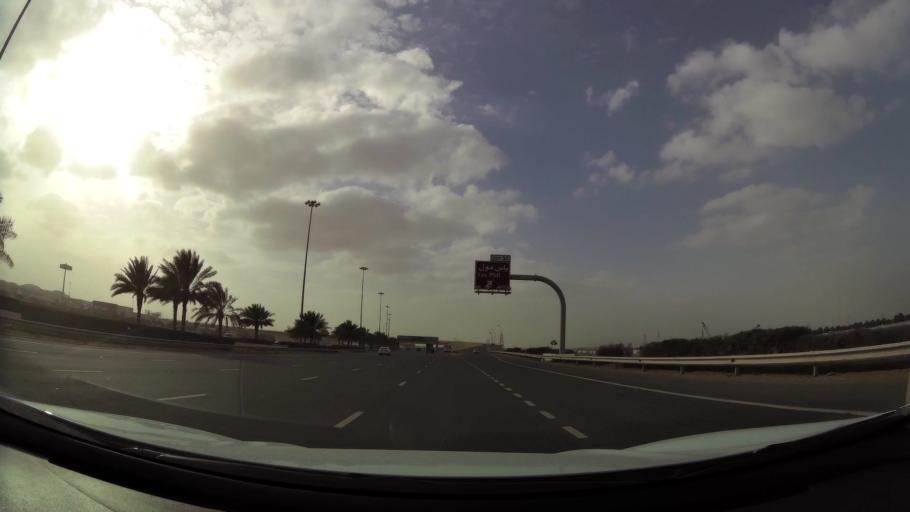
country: AE
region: Abu Dhabi
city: Abu Dhabi
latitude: 24.4936
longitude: 54.6176
